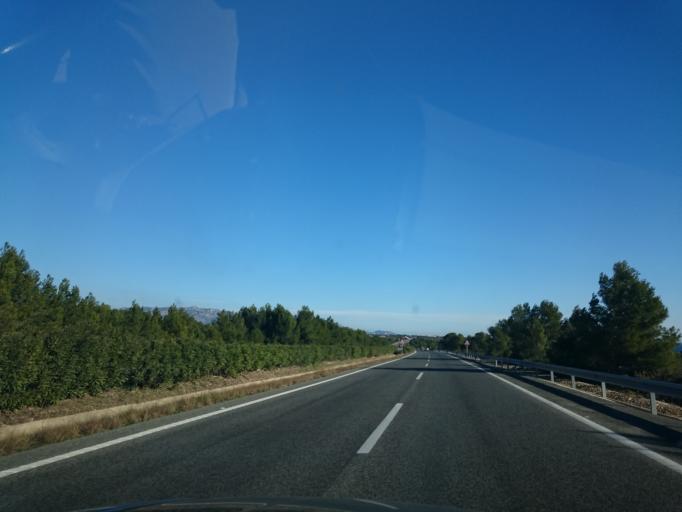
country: ES
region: Catalonia
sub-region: Provincia de Tarragona
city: El Perello
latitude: 40.8525
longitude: 0.7605
